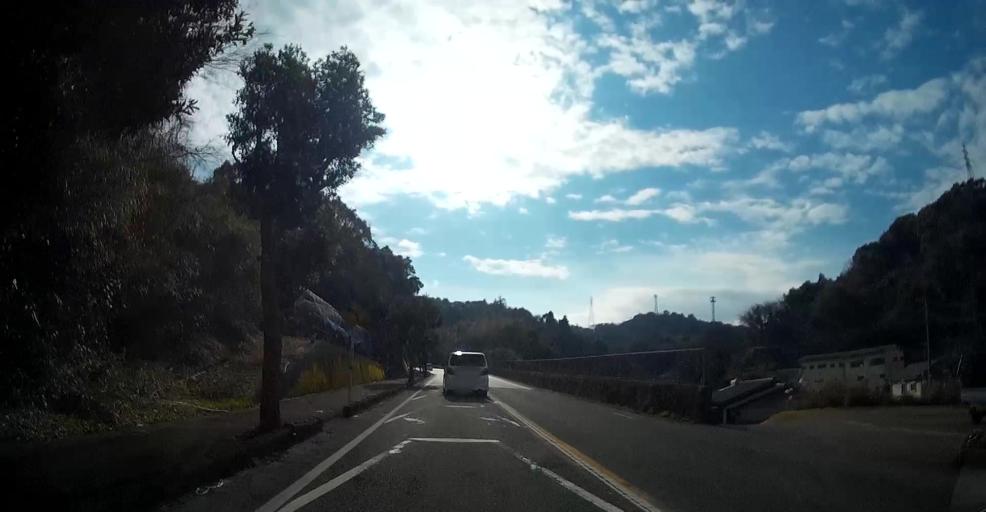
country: JP
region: Kumamoto
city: Yatsushiro
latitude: 32.6013
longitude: 130.4367
